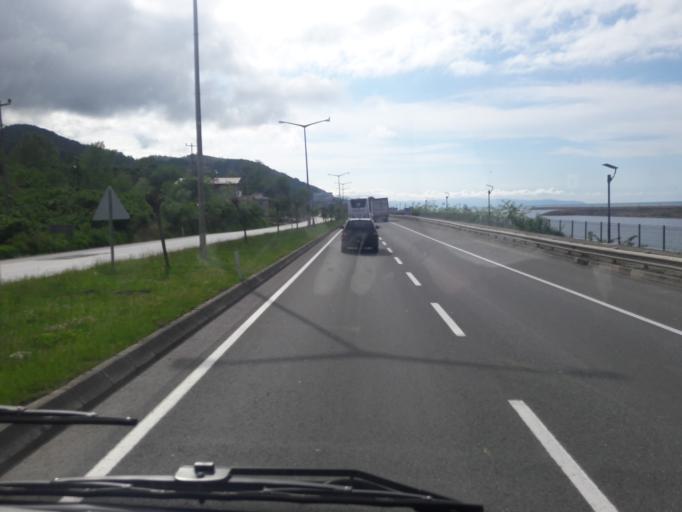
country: TR
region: Ordu
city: Gulyali
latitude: 40.9651
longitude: 38.0717
